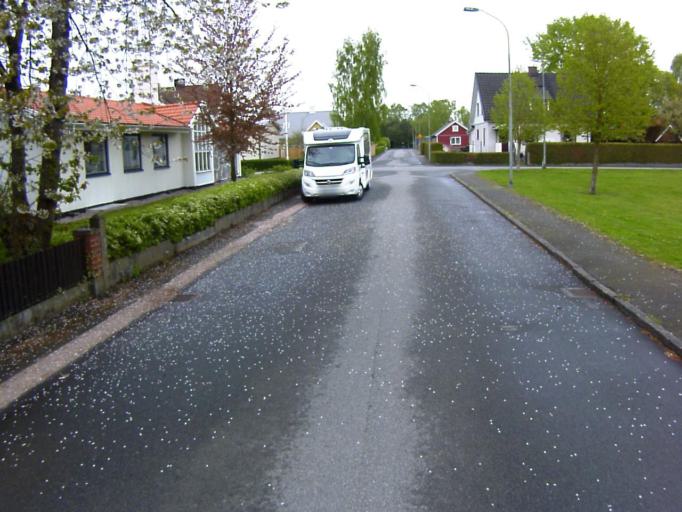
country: SE
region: Skane
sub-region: Kristianstads Kommun
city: Onnestad
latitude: 55.9324
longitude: 13.9702
